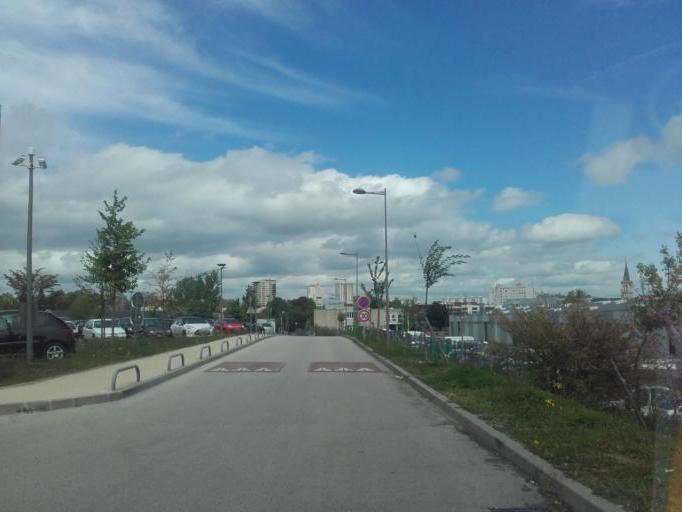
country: FR
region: Bourgogne
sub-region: Departement de Saone-et-Loire
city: Chalon-sur-Saone
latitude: 46.7768
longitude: 4.8424
